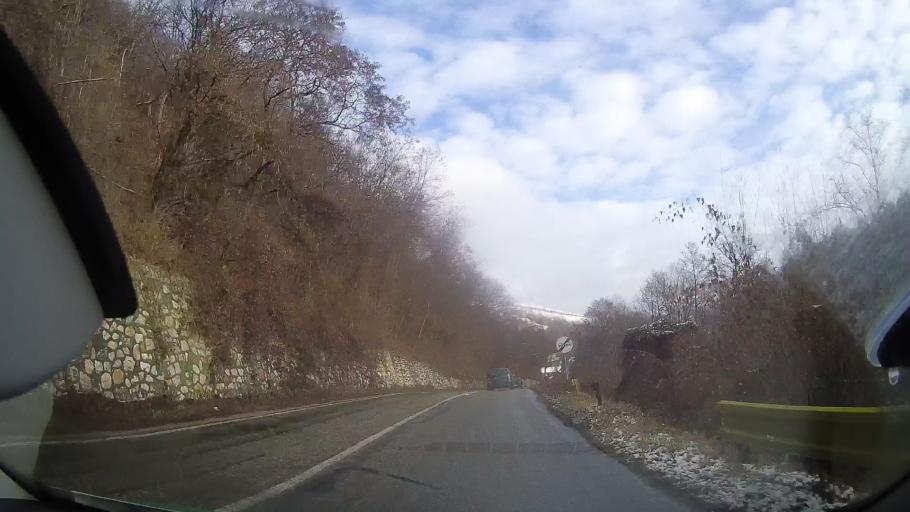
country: RO
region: Alba
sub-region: Oras Baia de Aries
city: Baia de Aries
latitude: 46.3890
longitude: 23.2809
